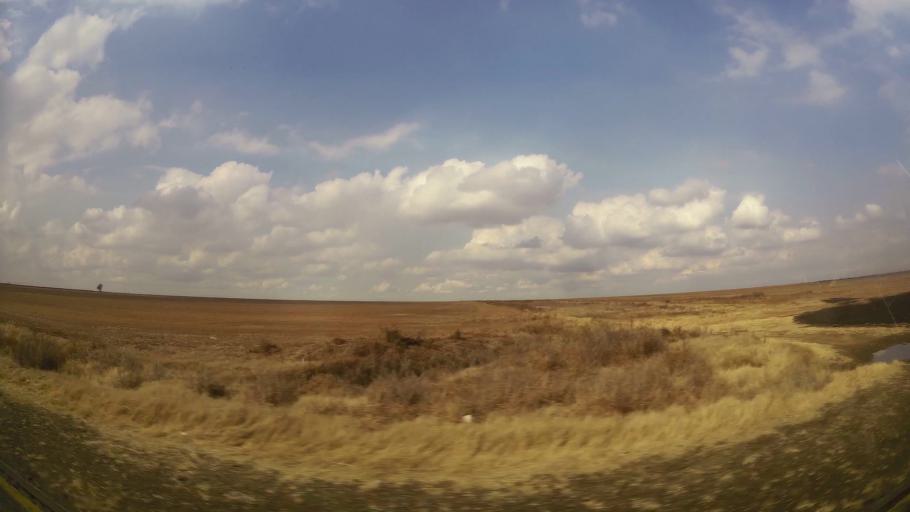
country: ZA
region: Orange Free State
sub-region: Fezile Dabi District Municipality
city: Sasolburg
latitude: -26.8382
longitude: 27.8945
